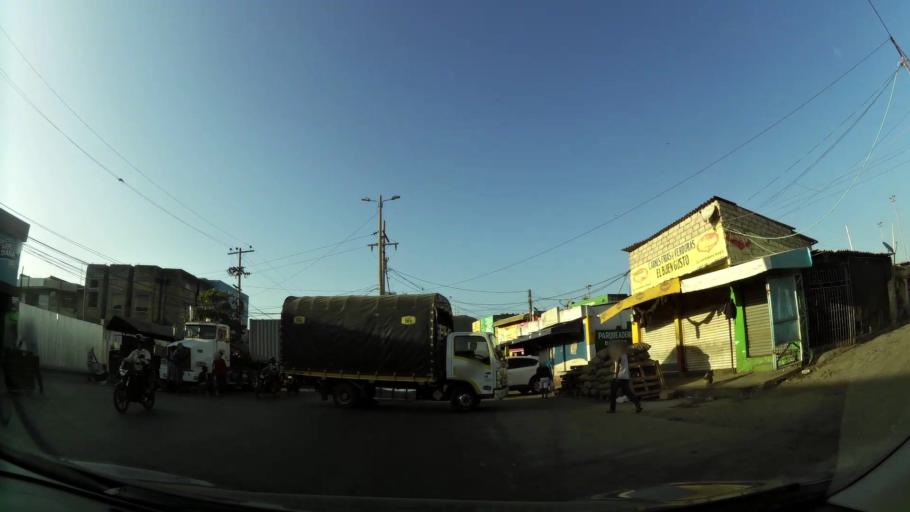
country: CO
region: Bolivar
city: Cartagena
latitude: 10.4112
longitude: -75.5224
